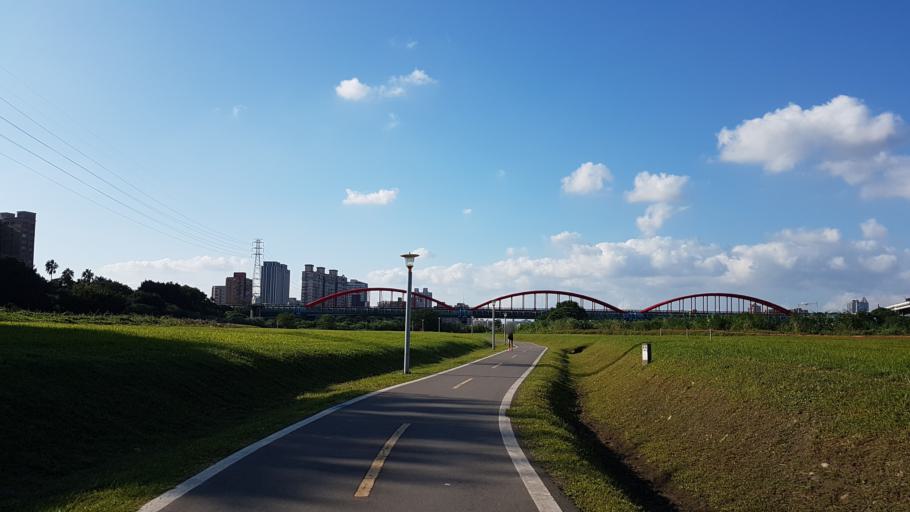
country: TW
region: Taipei
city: Taipei
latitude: 25.0080
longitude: 121.5294
